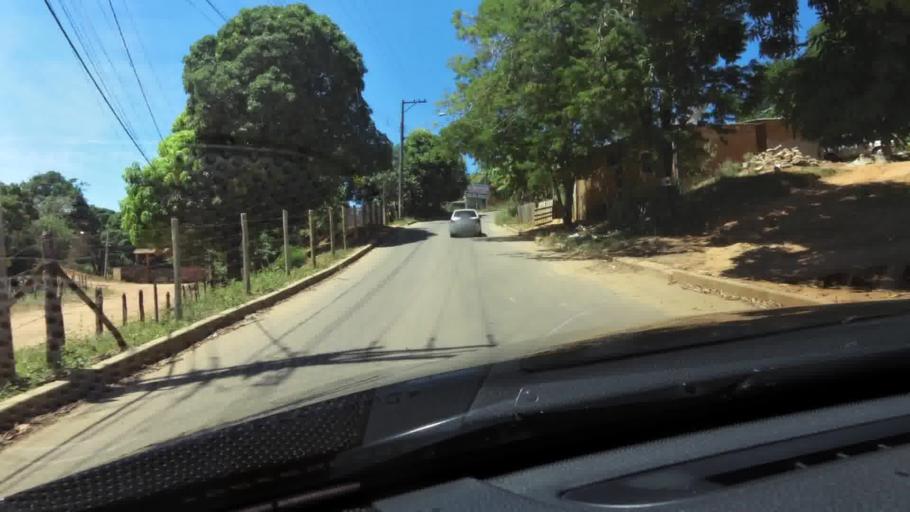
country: BR
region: Espirito Santo
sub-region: Guarapari
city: Guarapari
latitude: -20.6183
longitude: -40.4663
